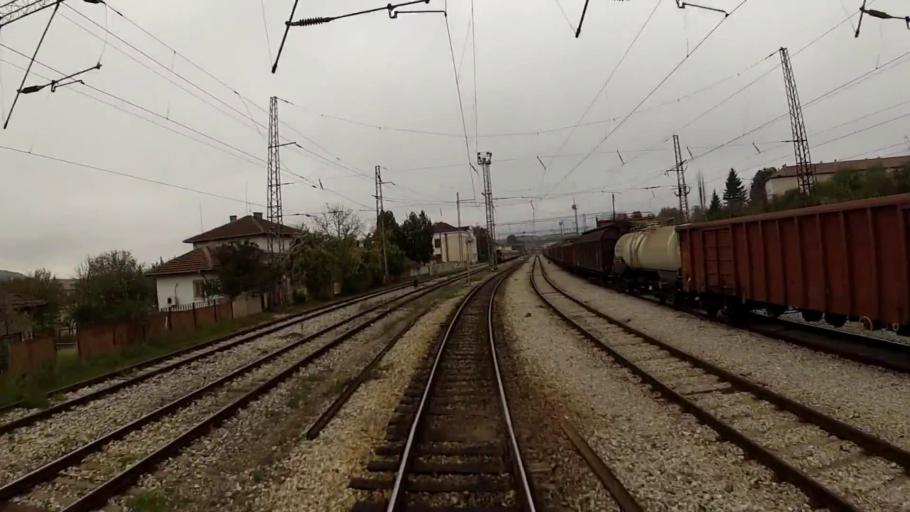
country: BG
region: Sofiya
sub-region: Obshtina Dragoman
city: Dragoman
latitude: 42.9274
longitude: 22.9329
